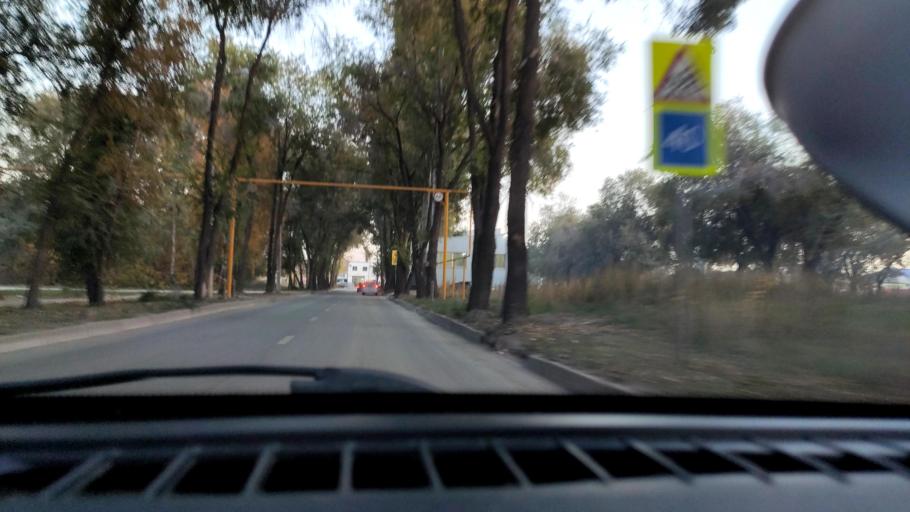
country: RU
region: Samara
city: Samara
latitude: 53.1993
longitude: 50.2451
